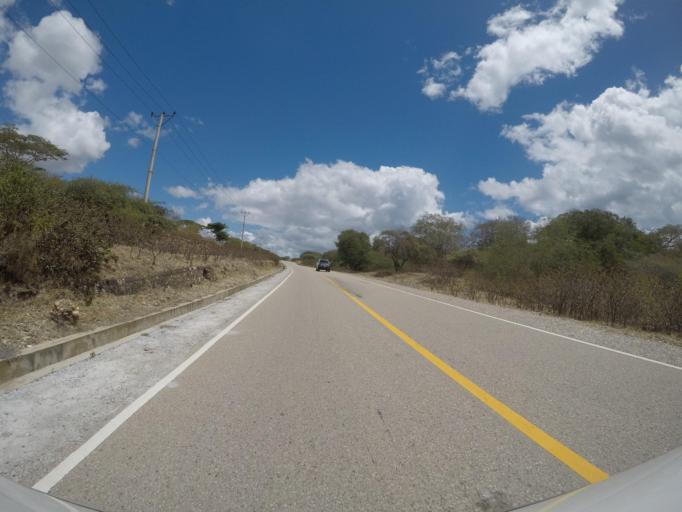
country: TL
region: Lautem
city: Lospalos
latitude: -8.4038
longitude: 126.8228
